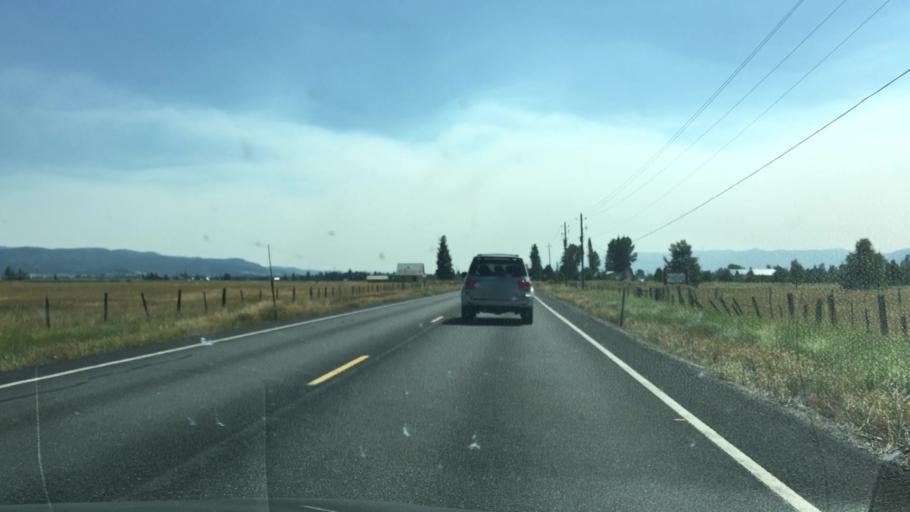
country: US
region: Idaho
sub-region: Valley County
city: McCall
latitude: 44.7504
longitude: -116.0783
